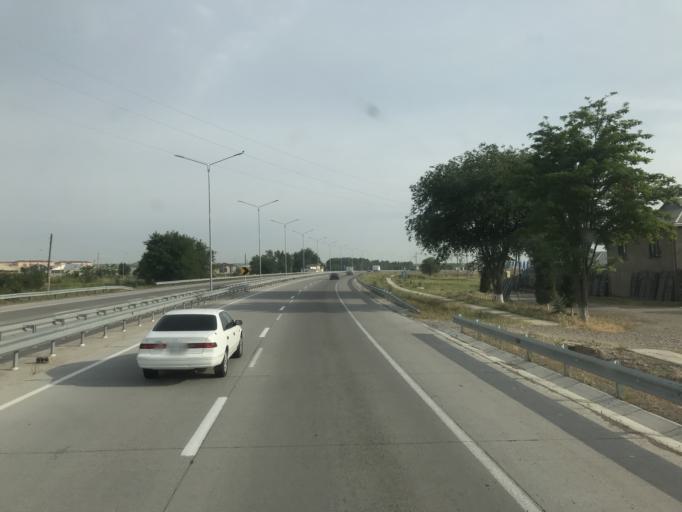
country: KZ
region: Ongtustik Qazaqstan
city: Qazyqurt
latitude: 41.7891
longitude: 69.3931
